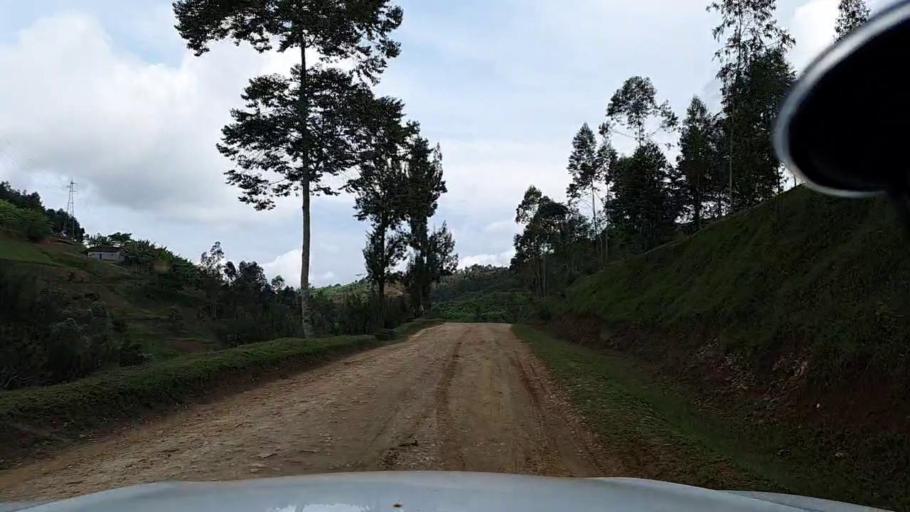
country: RW
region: Western Province
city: Kibuye
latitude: -2.1493
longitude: 29.5350
